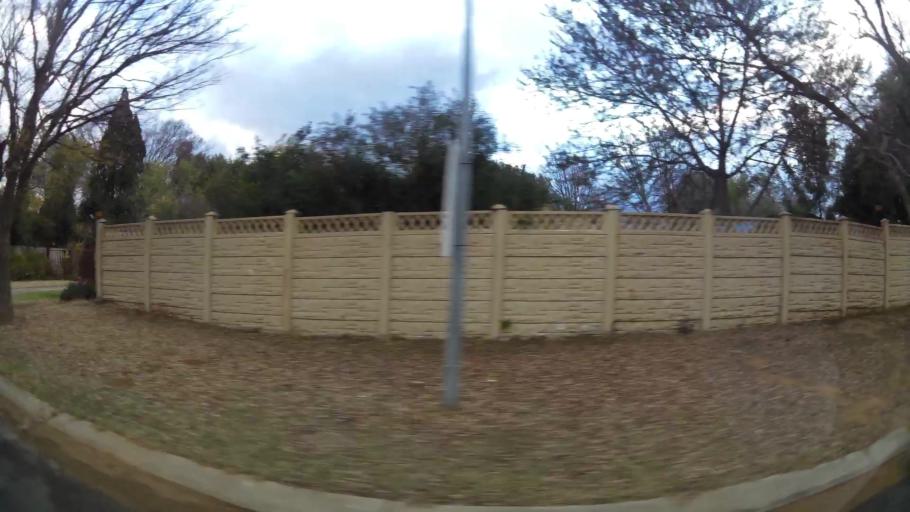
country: ZA
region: Orange Free State
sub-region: Lejweleputswa District Municipality
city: Welkom
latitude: -27.9543
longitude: 26.7410
